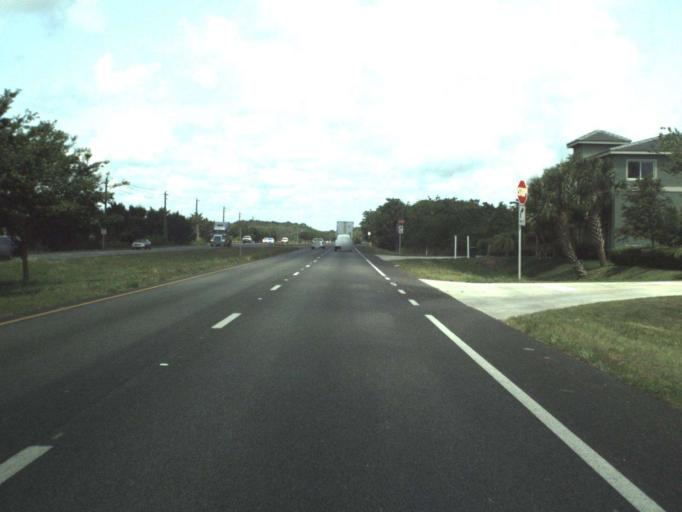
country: US
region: Florida
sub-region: Volusia County
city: Ormond Beach
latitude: 29.2950
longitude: -81.0774
